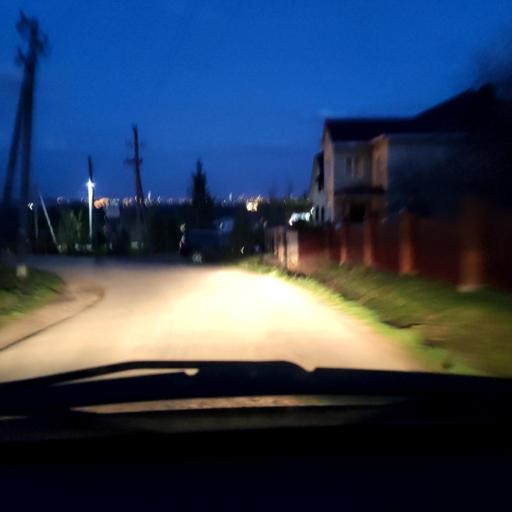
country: RU
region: Bashkortostan
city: Mikhaylovka
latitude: 54.8096
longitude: 55.8927
